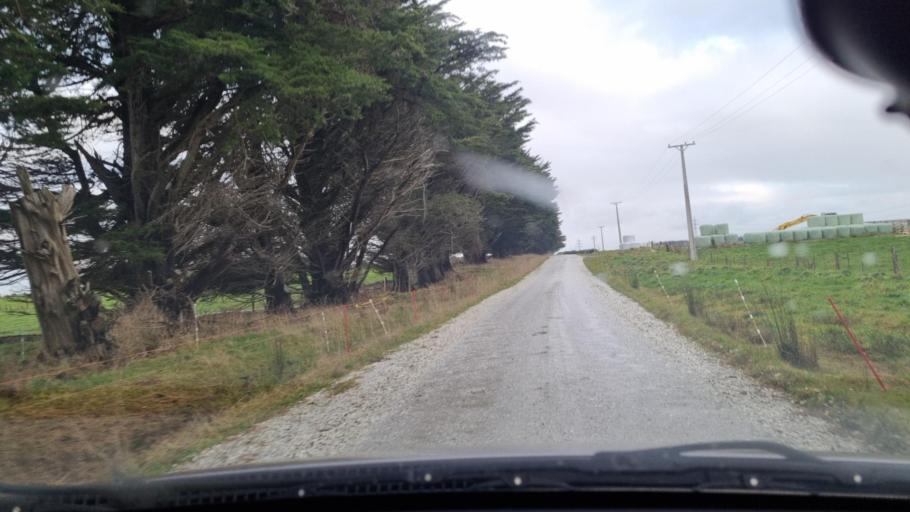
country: NZ
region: Southland
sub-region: Invercargill City
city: Invercargill
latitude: -46.4196
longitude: 168.4445
